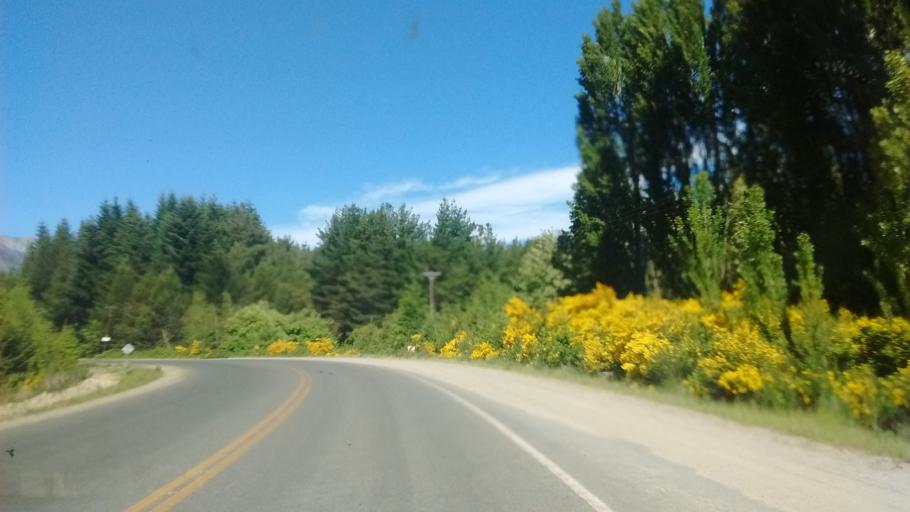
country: AR
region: Chubut
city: Hoyo de Epuyen
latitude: -42.0353
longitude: -71.5626
